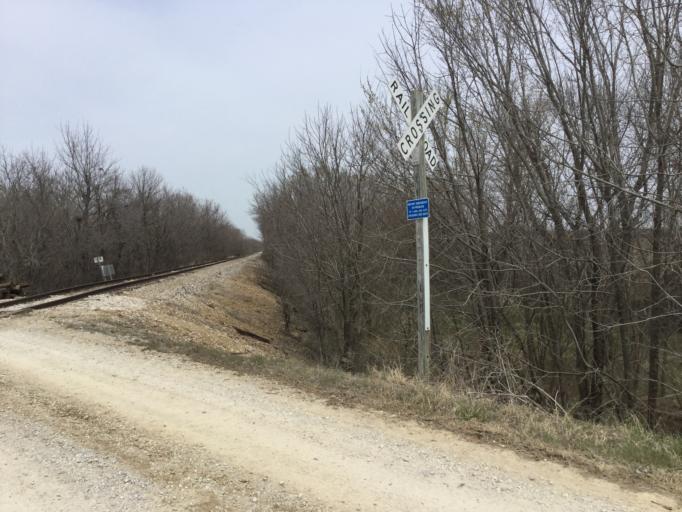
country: US
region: Kansas
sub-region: Wilson County
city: Fredonia
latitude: 37.4633
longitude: -95.8885
